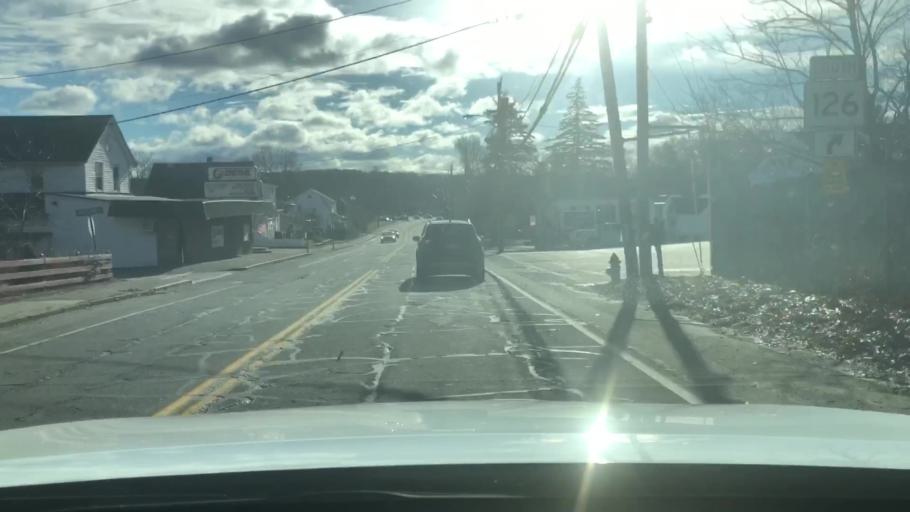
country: US
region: Rhode Island
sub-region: Providence County
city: Woonsocket
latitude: 42.0282
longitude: -71.4912
